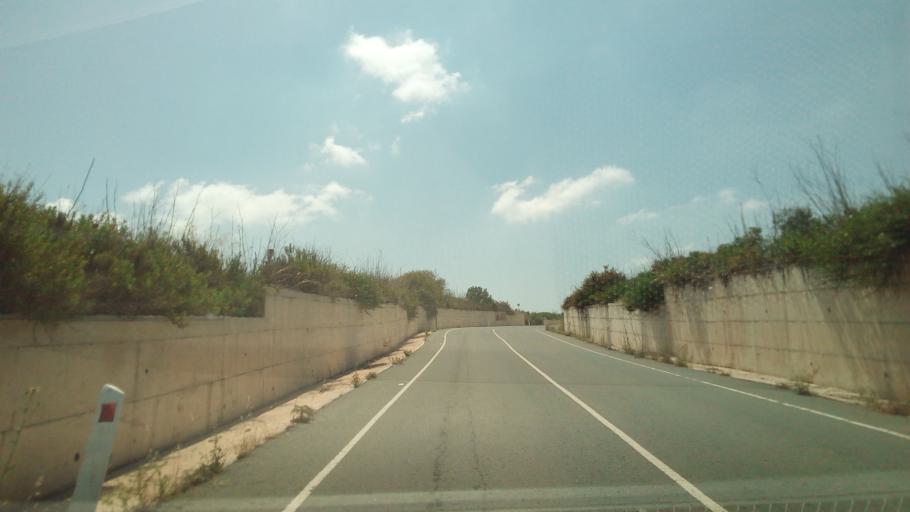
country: CY
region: Pafos
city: Tala
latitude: 34.9307
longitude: 32.5212
